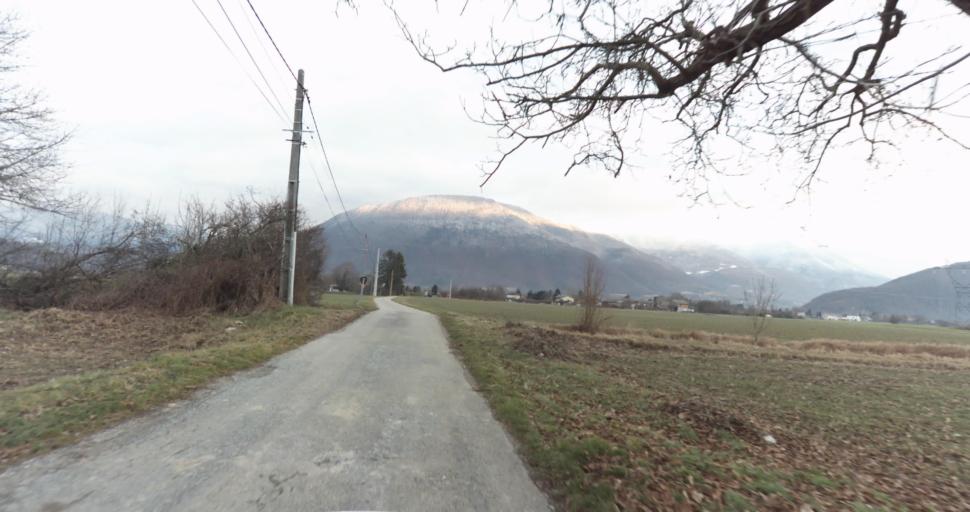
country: FR
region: Rhone-Alpes
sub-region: Departement de l'Isere
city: Vif
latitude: 45.0751
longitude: 5.6901
